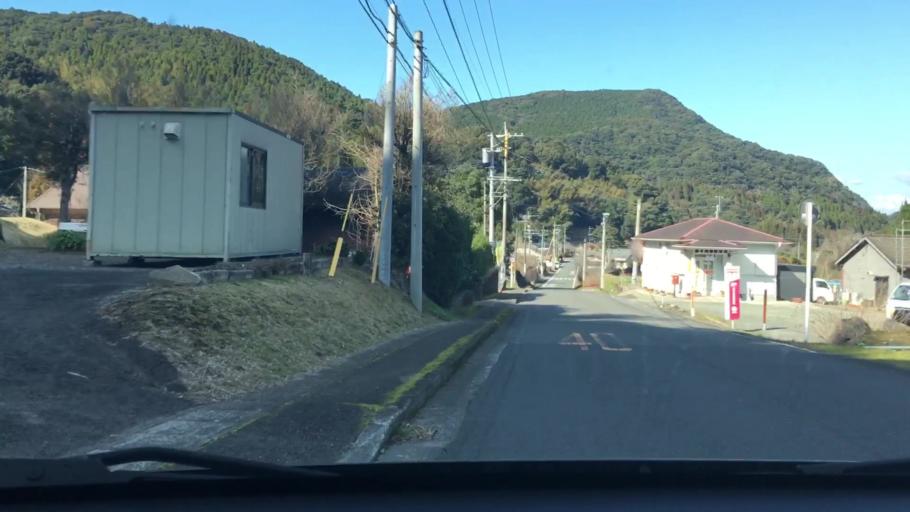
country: JP
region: Kagoshima
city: Ijuin
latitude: 31.7395
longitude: 130.4107
